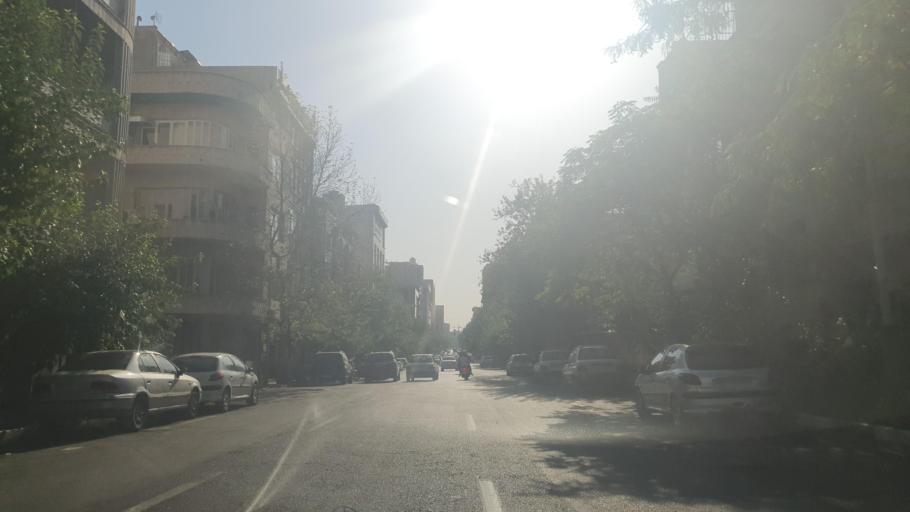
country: IR
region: Tehran
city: Tehran
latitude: 35.7056
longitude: 51.4231
